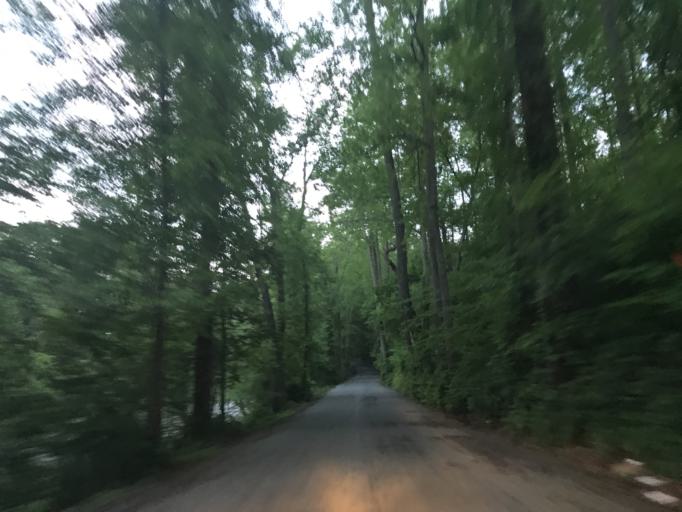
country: US
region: Maryland
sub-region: Harford County
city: Joppatowne
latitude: 39.4678
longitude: -76.3340
